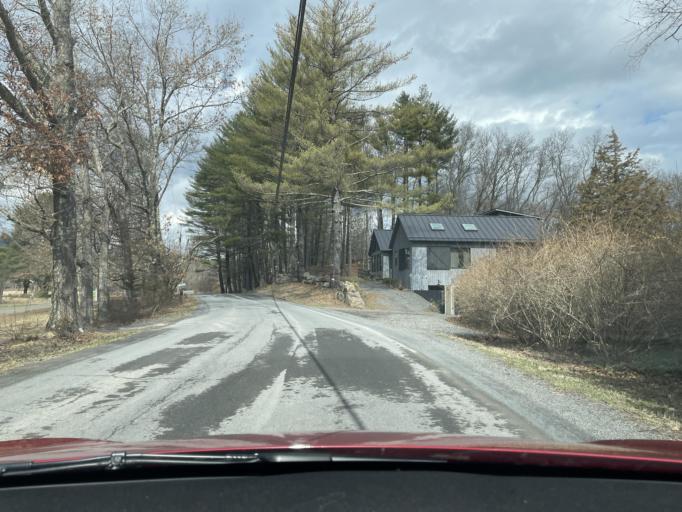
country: US
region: New York
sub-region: Ulster County
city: Zena
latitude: 42.0196
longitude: -74.0740
